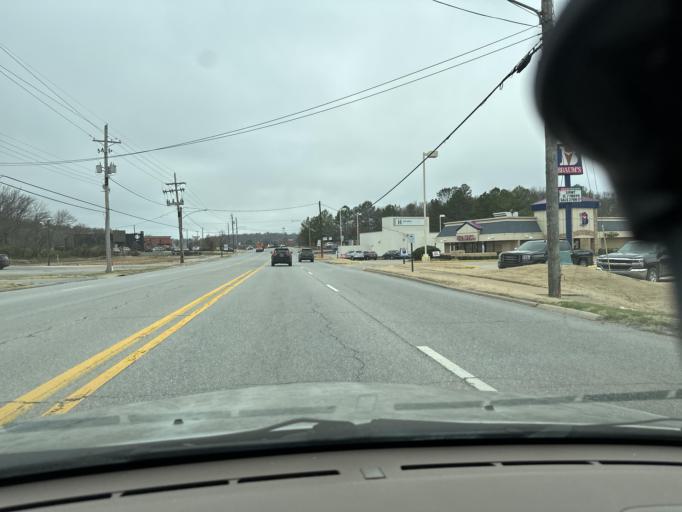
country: US
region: Arkansas
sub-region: Washington County
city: Fayetteville
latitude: 36.0979
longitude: -94.1514
